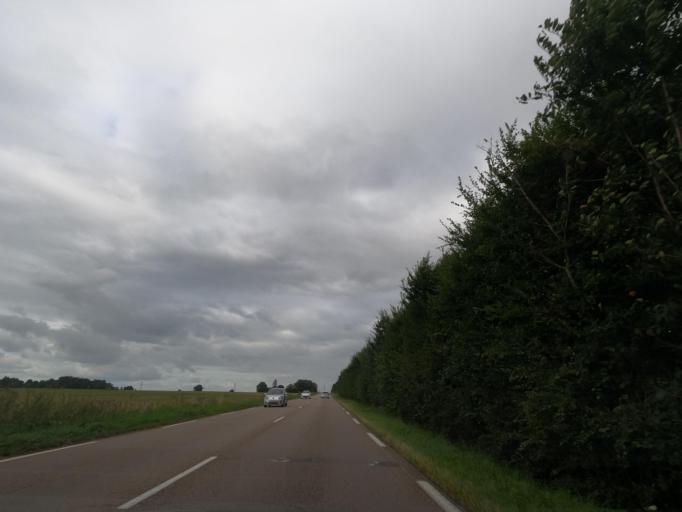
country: FR
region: Haute-Normandie
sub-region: Departement de l'Eure
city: Bourgtheroulde-Infreville
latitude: 49.2844
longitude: 0.8415
